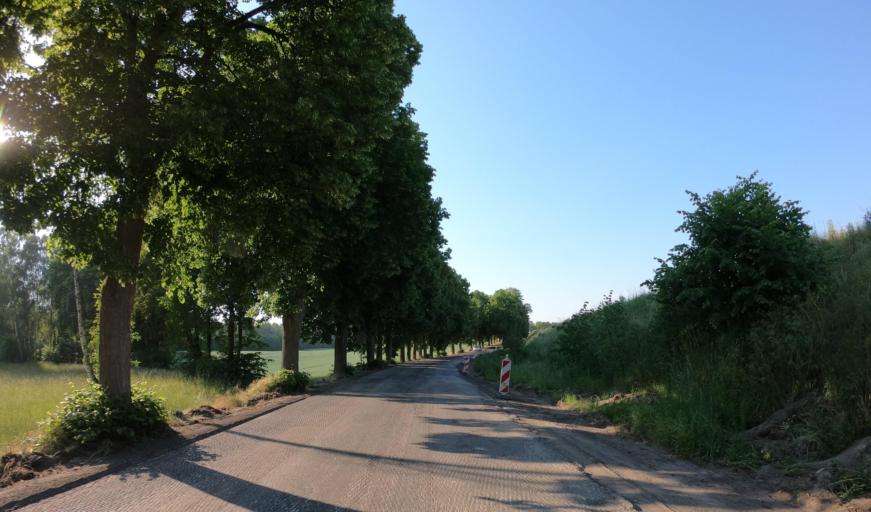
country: PL
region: West Pomeranian Voivodeship
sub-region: Powiat lobeski
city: Dobra
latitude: 53.5568
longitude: 15.3053
